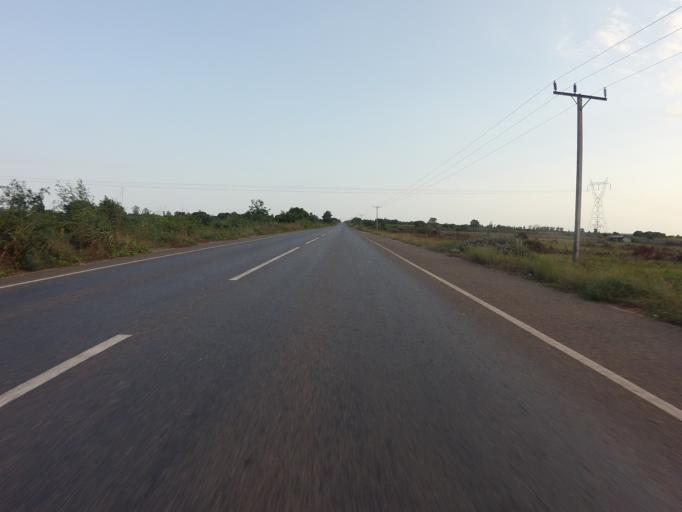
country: GH
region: Volta
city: Anloga
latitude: 6.0701
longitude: 0.6044
